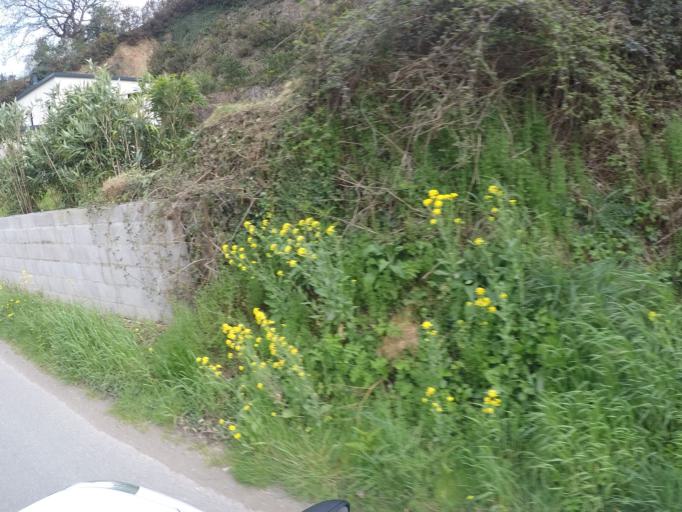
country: FR
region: Brittany
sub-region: Departement des Cotes-d'Armor
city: Plouezec
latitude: 48.7285
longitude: -2.9504
